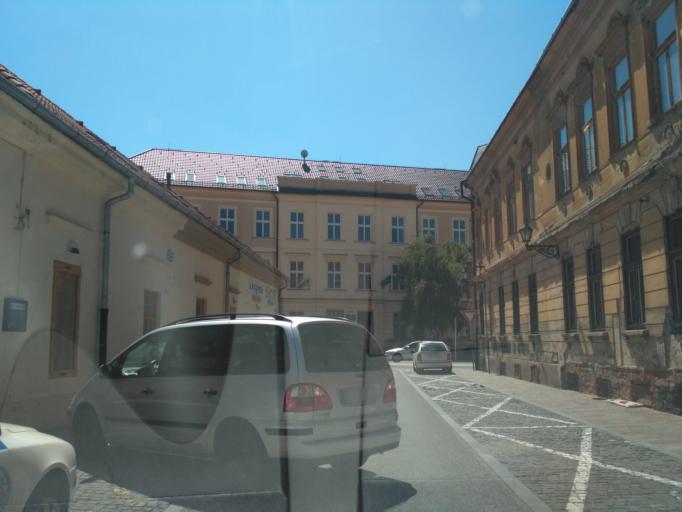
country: SK
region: Kosicky
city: Kosice
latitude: 48.7186
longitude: 21.2570
